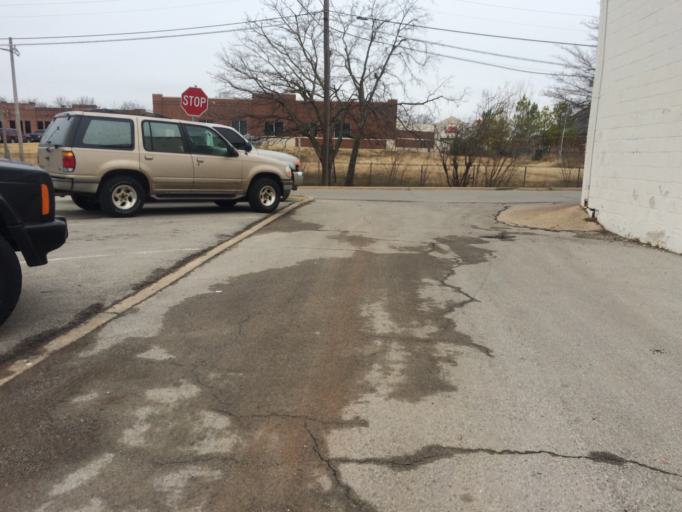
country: US
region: Oklahoma
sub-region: Cleveland County
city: Norman
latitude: 35.2176
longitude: -97.4513
